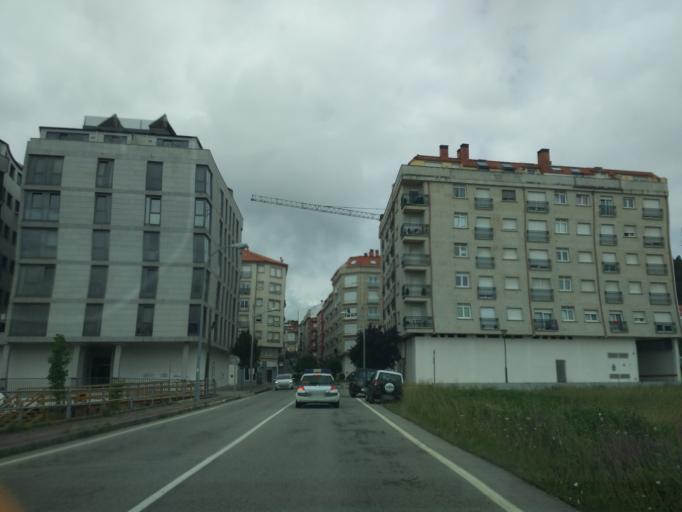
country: ES
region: Galicia
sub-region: Provincia da Coruna
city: Boiro
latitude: 42.6477
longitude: -8.8779
